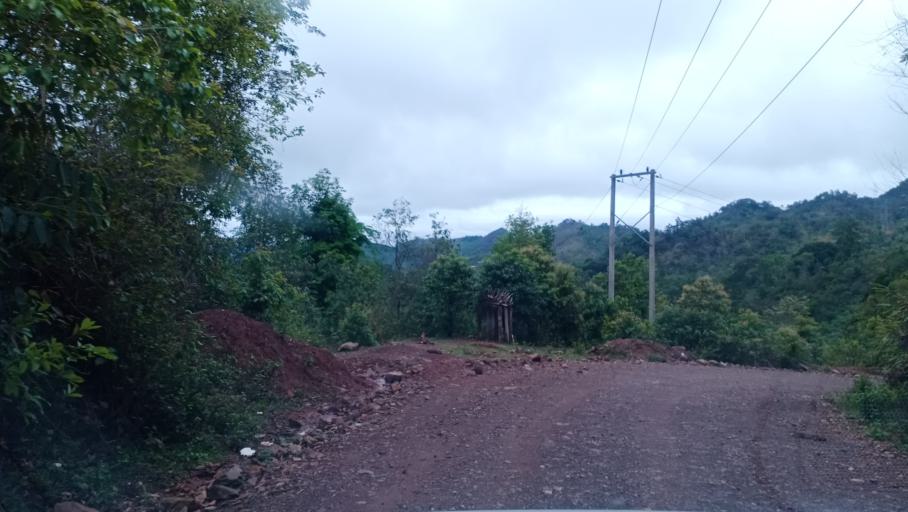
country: LA
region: Phongsali
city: Phongsali
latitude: 21.3400
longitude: 102.0827
